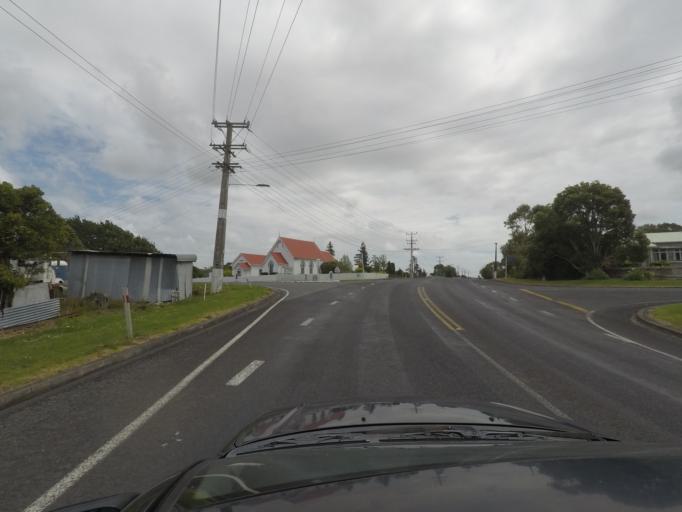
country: NZ
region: Auckland
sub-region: Auckland
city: Parakai
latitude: -36.6263
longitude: 174.5018
